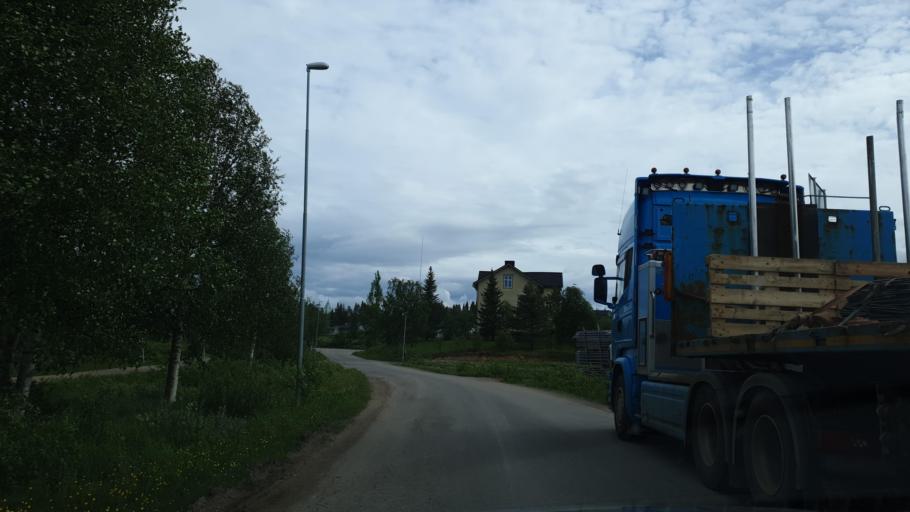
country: SE
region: Norrbotten
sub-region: Gallivare Kommun
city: Gaellivare
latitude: 67.1287
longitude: 20.6496
